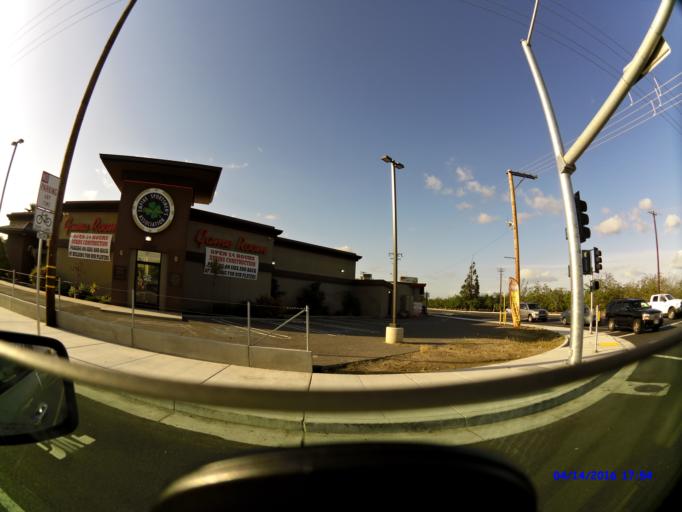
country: US
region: California
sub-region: Stanislaus County
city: Del Rio
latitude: 37.7112
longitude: -120.9952
